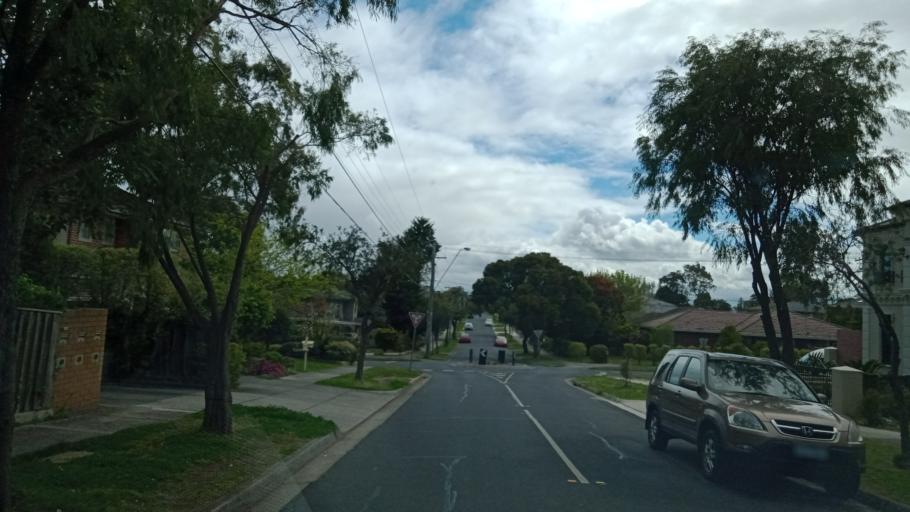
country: AU
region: Victoria
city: Burwood East
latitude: -37.8677
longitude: 145.1381
